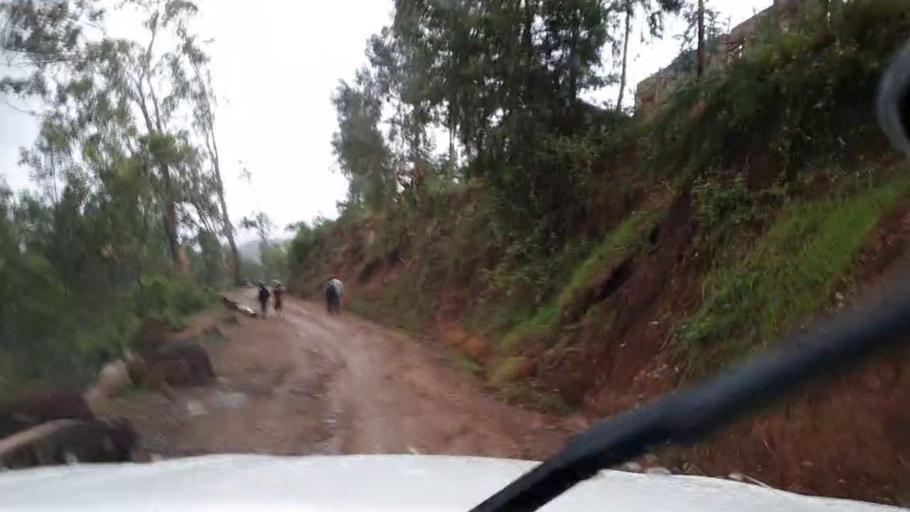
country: BI
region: Kayanza
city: Kayanza
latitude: -2.7841
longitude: 29.5328
